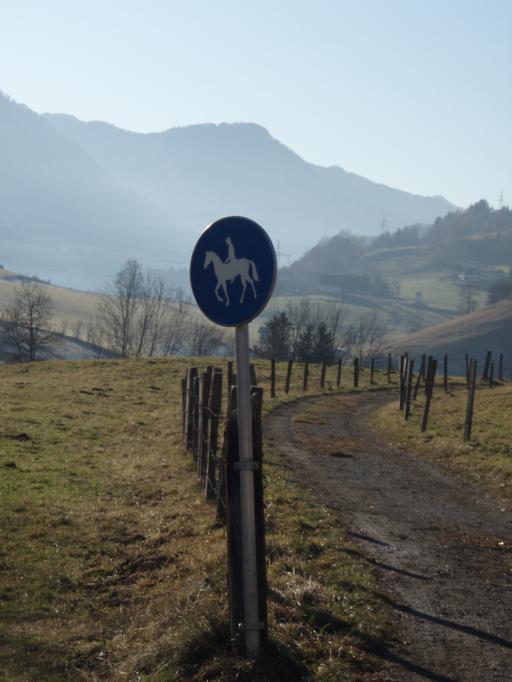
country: AT
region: Salzburg
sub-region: Politischer Bezirk Sankt Johann im Pongau
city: Sankt Veit im Pongau
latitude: 47.3280
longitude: 13.1475
